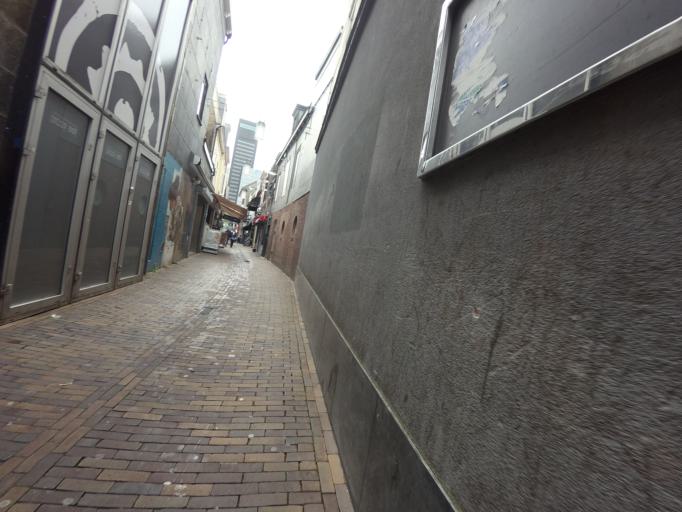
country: NL
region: Friesland
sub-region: Gemeente Leeuwarden
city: Bilgaard
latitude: 53.2008
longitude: 5.7927
